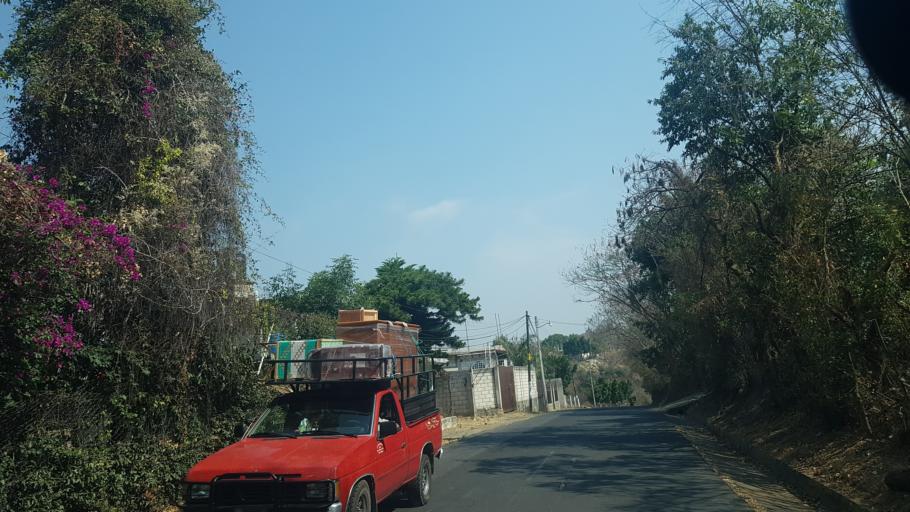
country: MX
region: Morelos
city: Tlacotepec
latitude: 18.8107
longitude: -98.7559
